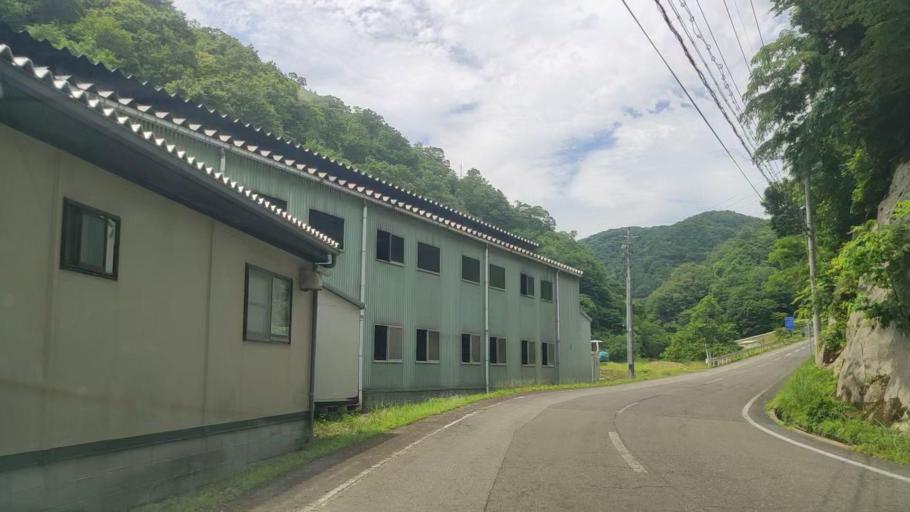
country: JP
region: Hyogo
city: Toyooka
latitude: 35.5230
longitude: 134.6980
